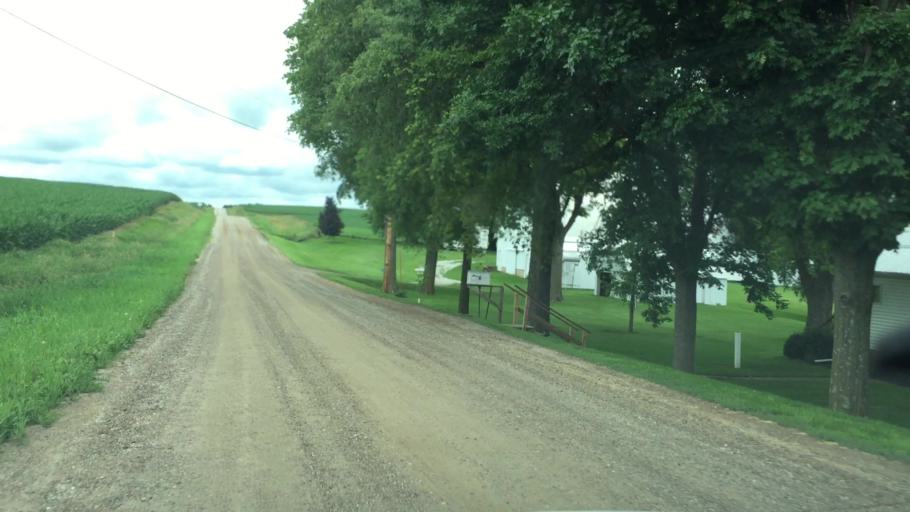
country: US
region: Iowa
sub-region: Jasper County
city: Monroe
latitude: 41.5953
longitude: -93.0970
